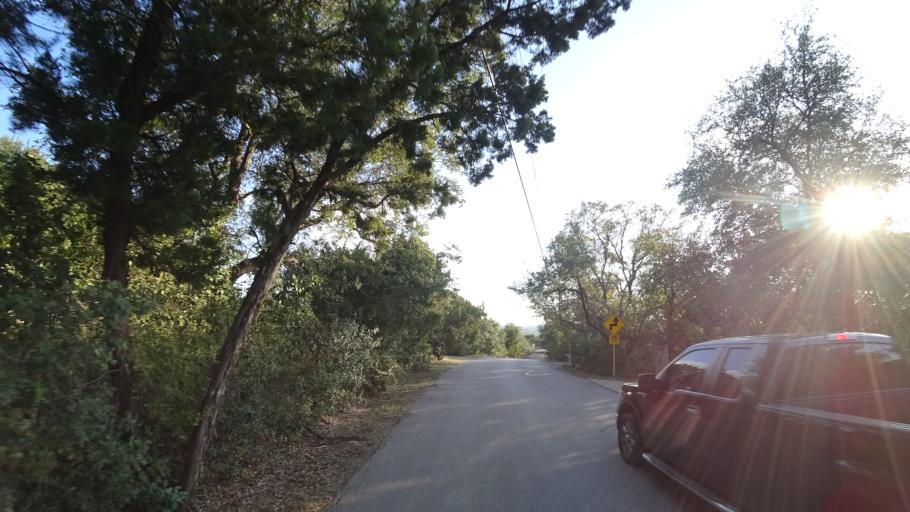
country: US
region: Texas
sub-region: Travis County
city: Lost Creek
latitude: 30.2968
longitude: -97.8408
